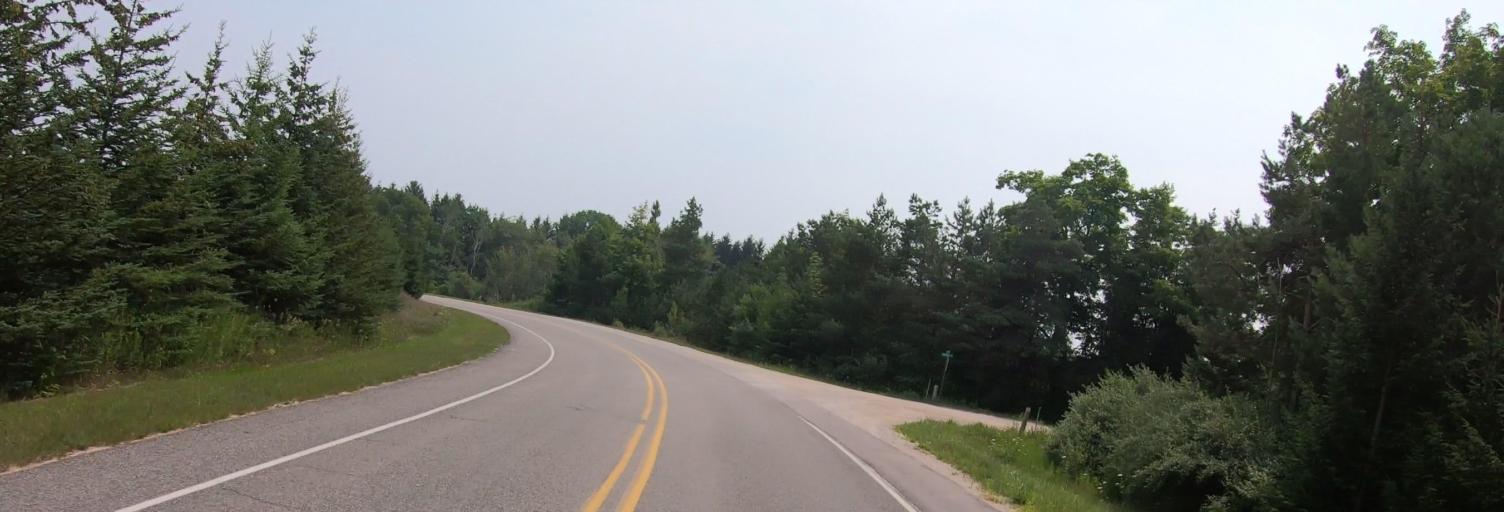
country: US
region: Michigan
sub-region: Leelanau County
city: Leland
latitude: 45.1908
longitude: -85.5453
